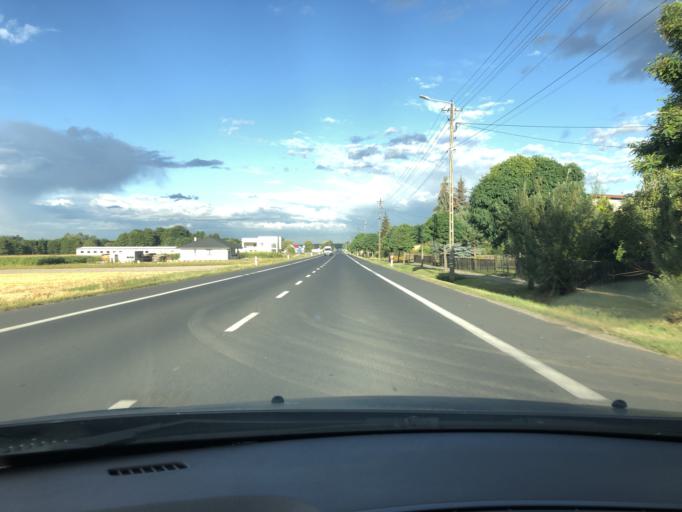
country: PL
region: Lodz Voivodeship
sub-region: Powiat wieruszowski
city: Galewice
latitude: 51.3035
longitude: 18.2734
